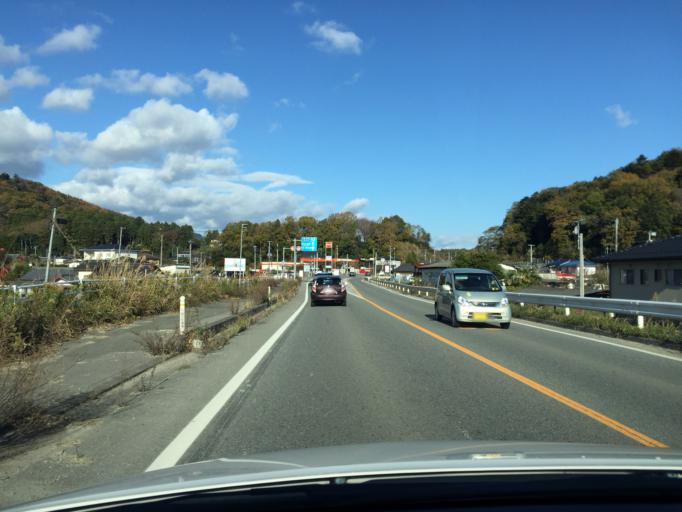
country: JP
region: Fukushima
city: Iwaki
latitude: 37.2019
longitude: 140.9937
